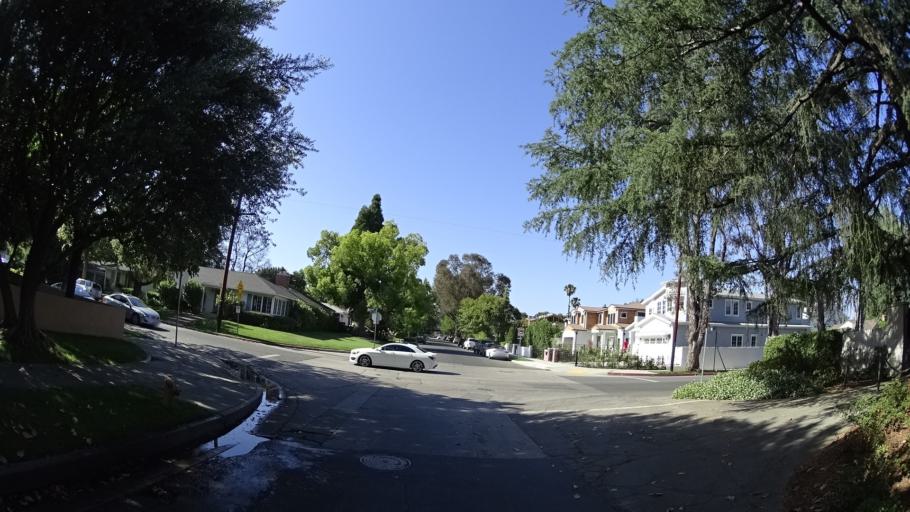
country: US
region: California
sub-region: Los Angeles County
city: Universal City
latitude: 34.1502
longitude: -118.3572
